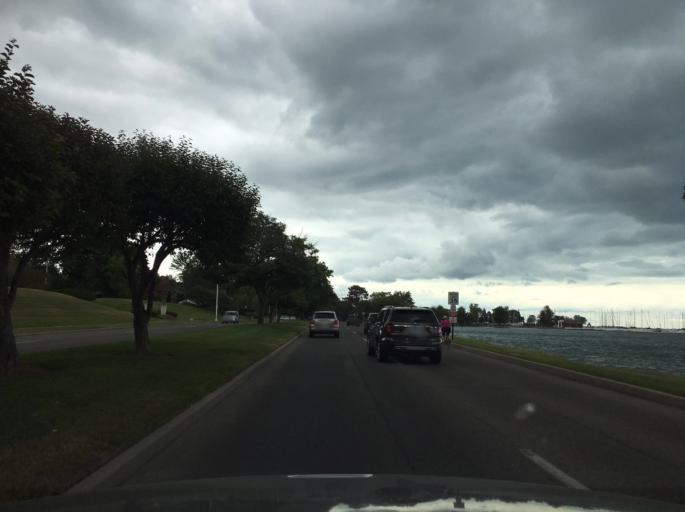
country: US
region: Michigan
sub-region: Wayne County
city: Grosse Pointe Farms
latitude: 42.3985
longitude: -82.8887
